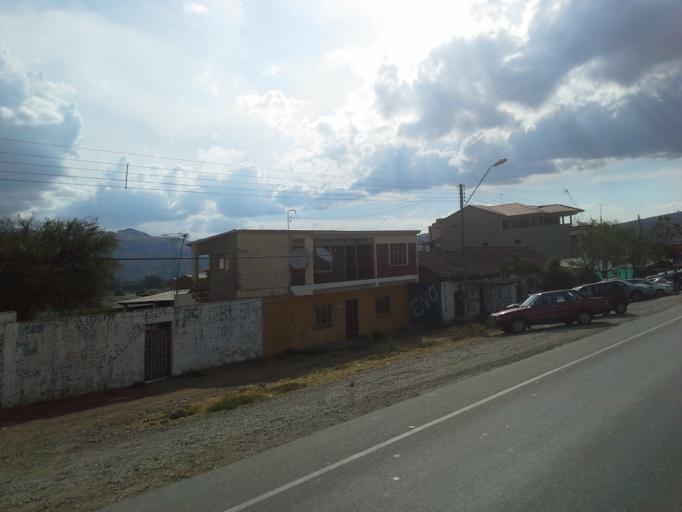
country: BO
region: Cochabamba
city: Tarata
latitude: -17.5376
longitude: -66.0729
